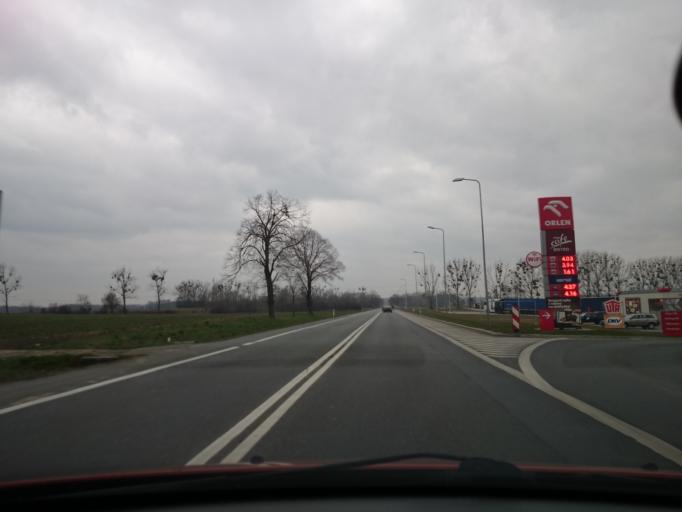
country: PL
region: Opole Voivodeship
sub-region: Powiat opolski
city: Chroscina
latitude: 50.6909
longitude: 17.7928
